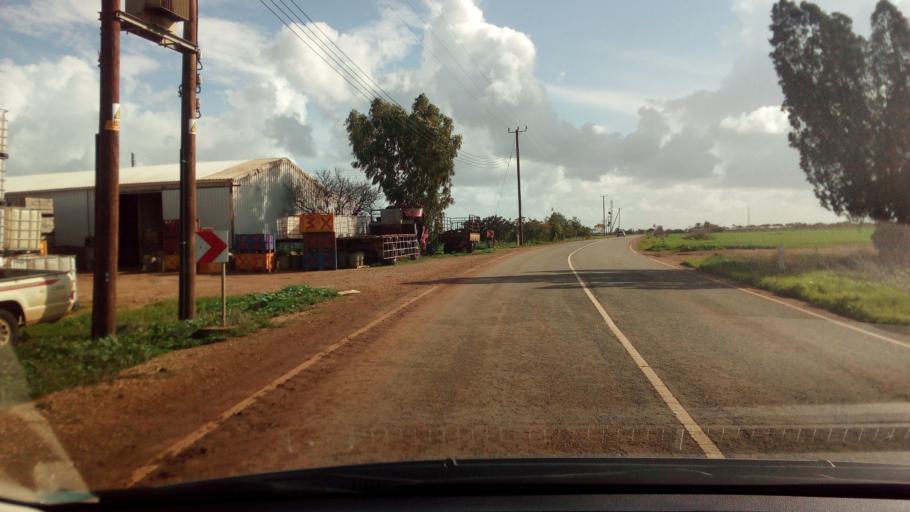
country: CY
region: Ammochostos
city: Achna
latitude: 35.0601
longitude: 33.8044
